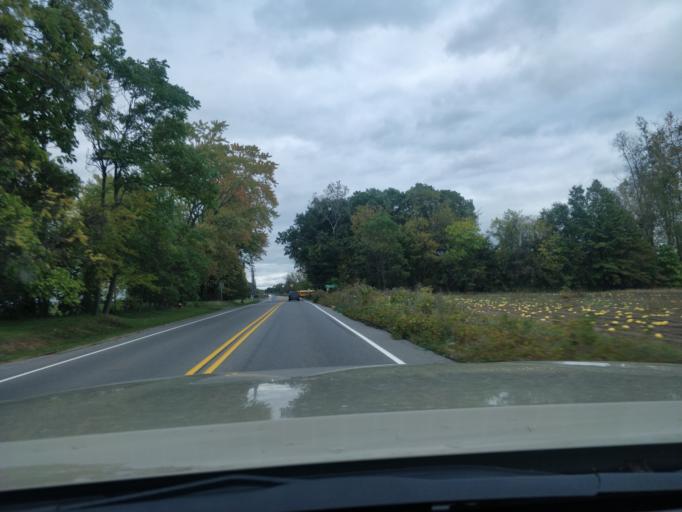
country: US
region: Michigan
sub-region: Wayne County
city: Taylor
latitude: 42.1812
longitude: -83.3090
